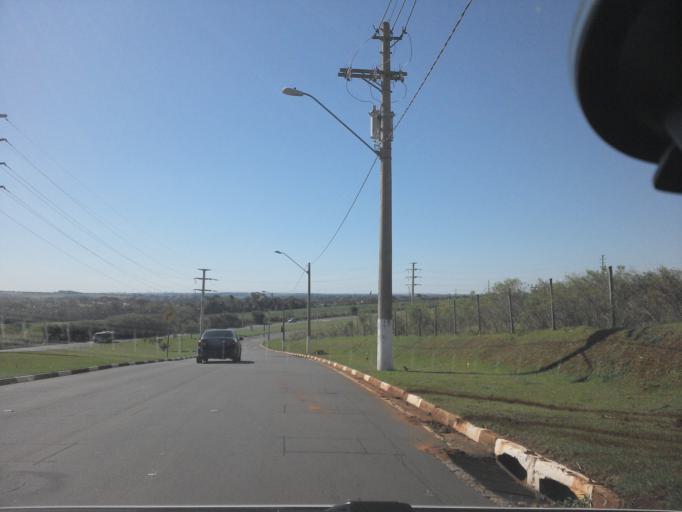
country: BR
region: Sao Paulo
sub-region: Campinas
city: Campinas
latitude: -22.8385
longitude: -47.0628
